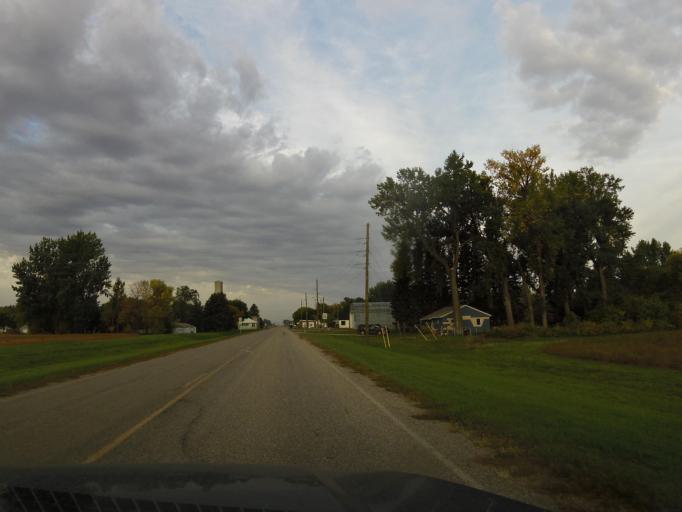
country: US
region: North Dakota
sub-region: Pembina County
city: Cavalier
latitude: 48.6882
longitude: -97.6627
